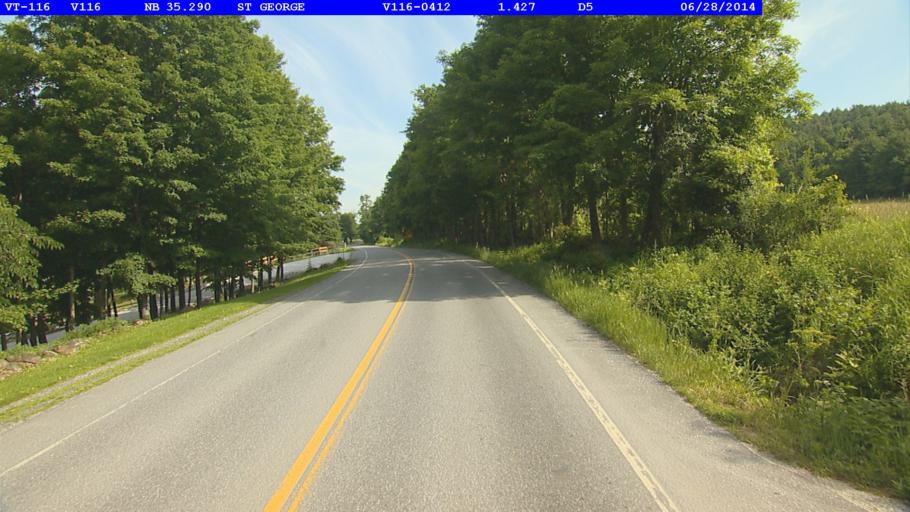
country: US
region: Vermont
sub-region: Chittenden County
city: Hinesburg
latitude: 44.3984
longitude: -73.1397
